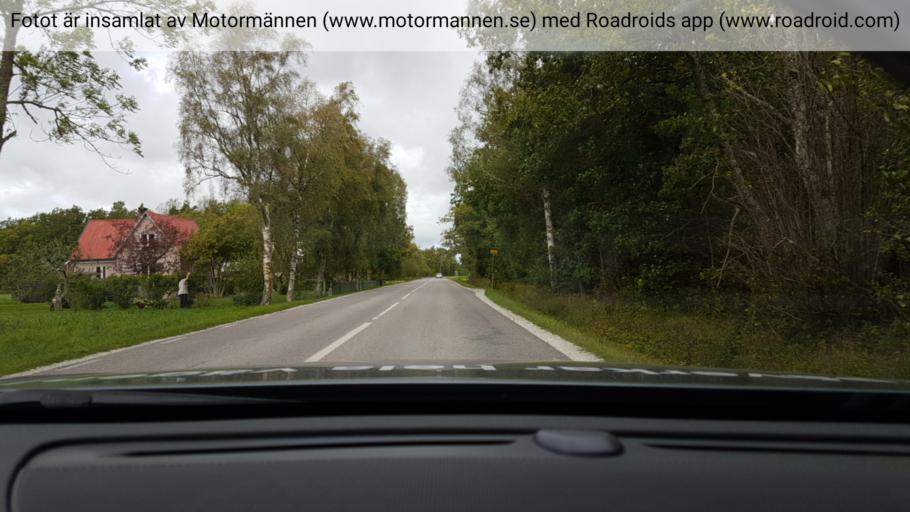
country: SE
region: Gotland
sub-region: Gotland
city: Klintehamn
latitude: 57.4307
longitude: 18.3669
